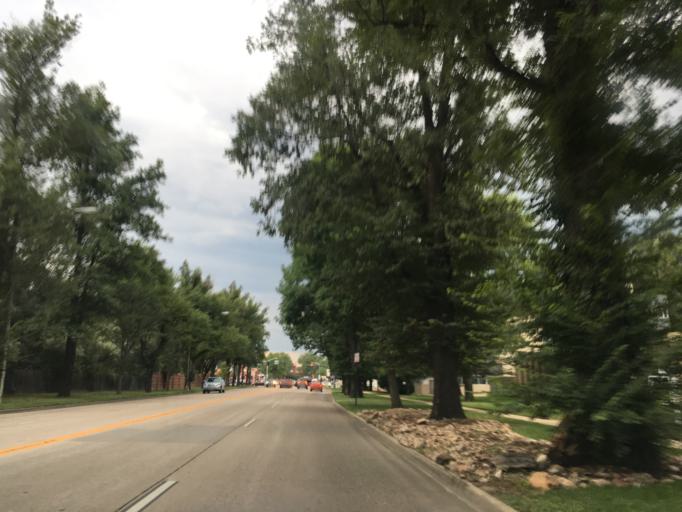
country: US
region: Colorado
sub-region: Arapahoe County
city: Glendale
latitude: 39.7055
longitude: -104.9594
